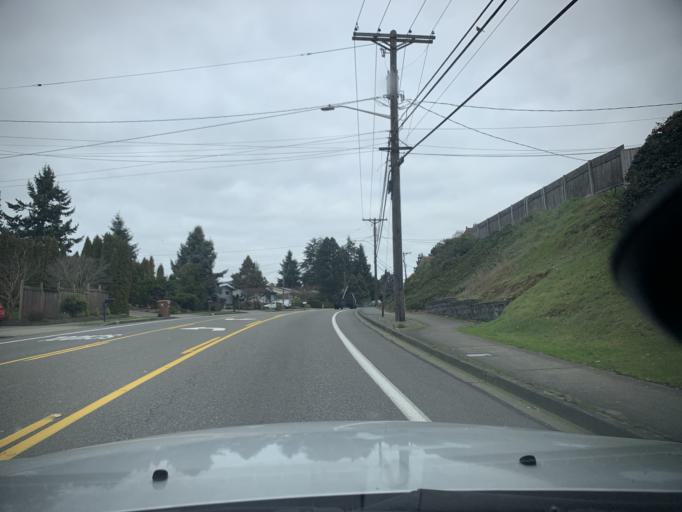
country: US
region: Washington
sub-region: Pierce County
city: Fircrest
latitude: 47.2703
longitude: -122.5305
